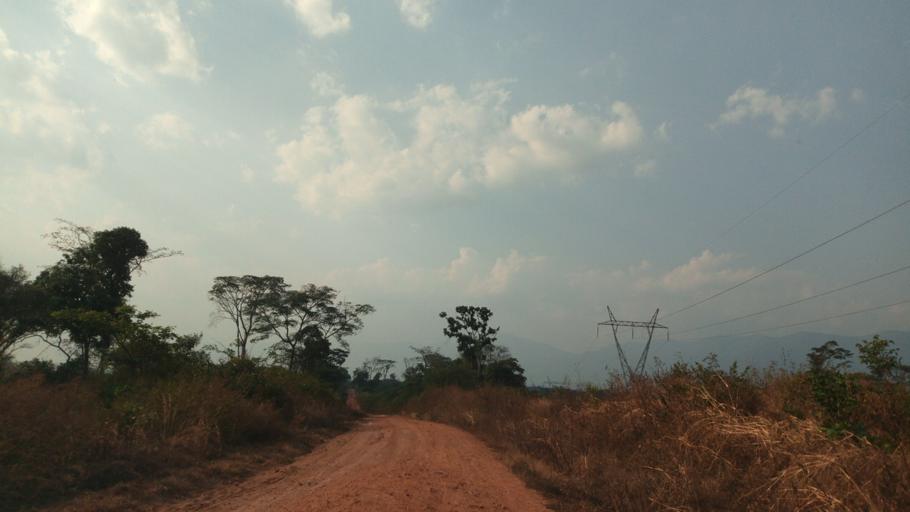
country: TZ
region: Kigoma
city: Kigoma
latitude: -5.1884
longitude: 28.8935
